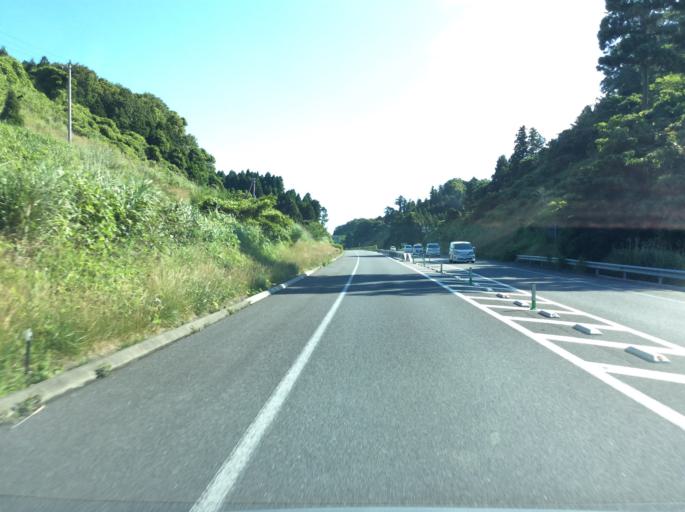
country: JP
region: Fukushima
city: Iwaki
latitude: 37.1835
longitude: 140.9820
